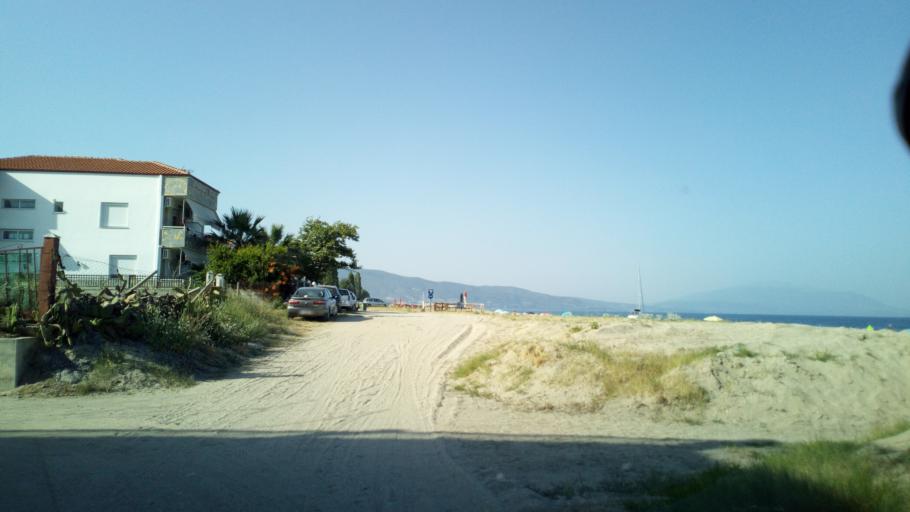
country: GR
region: Central Macedonia
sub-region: Nomos Thessalonikis
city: Nea Vrasna
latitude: 40.7026
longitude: 23.7000
